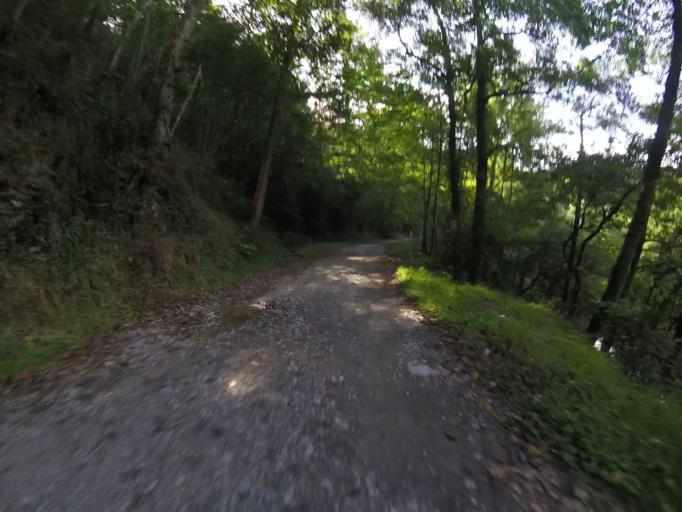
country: ES
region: Basque Country
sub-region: Provincia de Guipuzcoa
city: Elduayen
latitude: 43.1769
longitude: -1.9863
